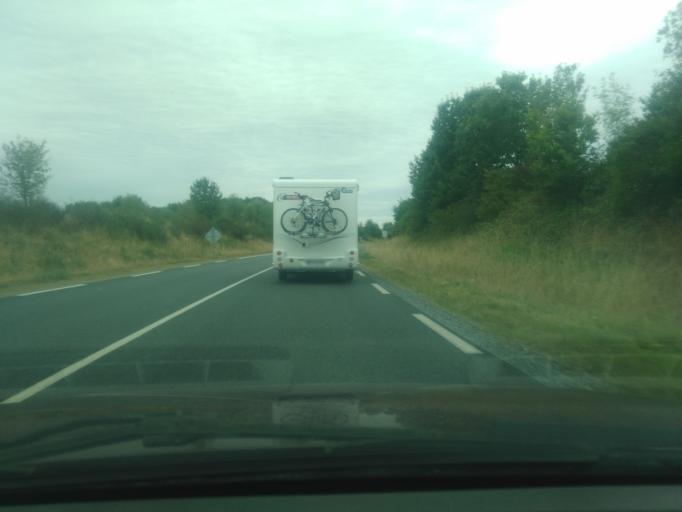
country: FR
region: Centre
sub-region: Departement de l'Indre
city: Saint-Marcel
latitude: 46.6086
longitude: 1.5227
